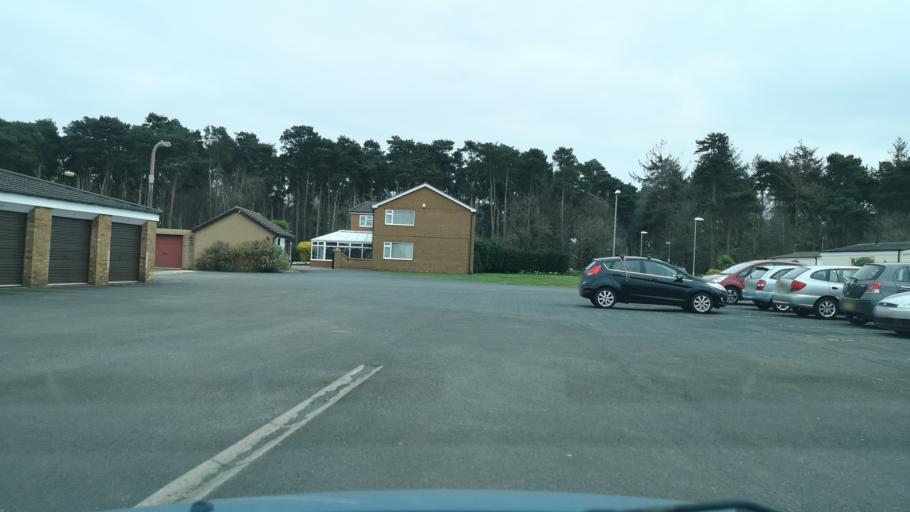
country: GB
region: England
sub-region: North Lincolnshire
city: Scunthorpe
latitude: 53.5699
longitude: -0.6868
